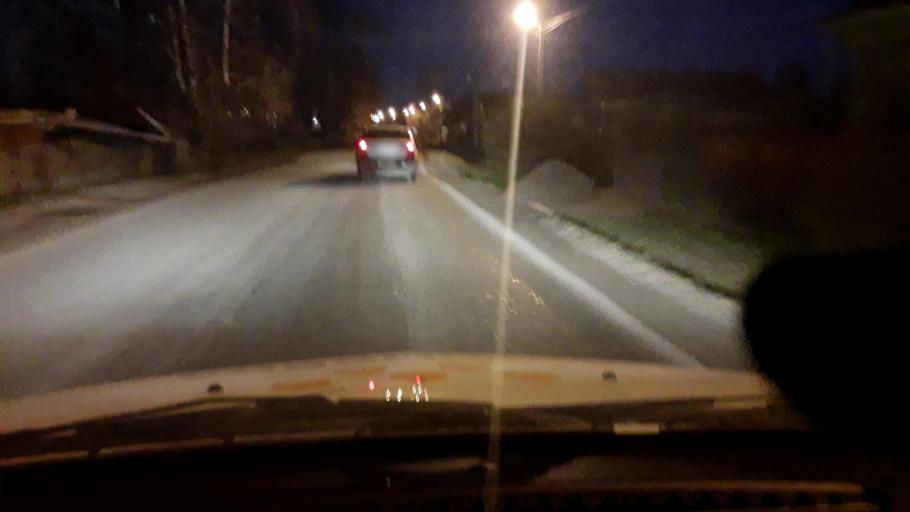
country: RU
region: Bashkortostan
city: Iglino
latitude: 54.7752
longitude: 56.2269
